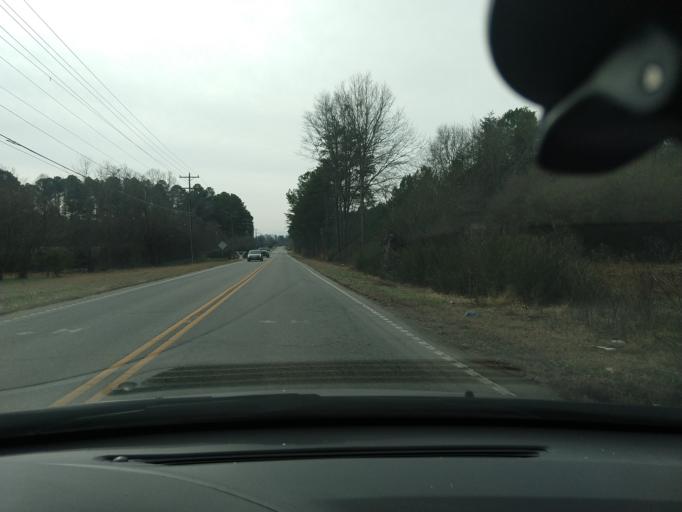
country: US
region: South Carolina
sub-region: Spartanburg County
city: Spartanburg
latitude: 34.9939
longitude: -81.8785
